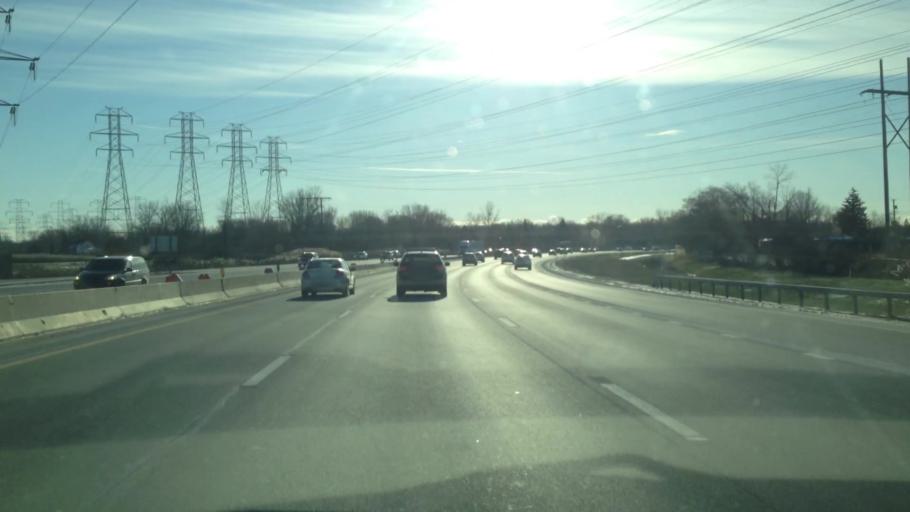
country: US
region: New York
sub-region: Erie County
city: Cheektowaga
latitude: 42.8823
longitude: -78.7694
